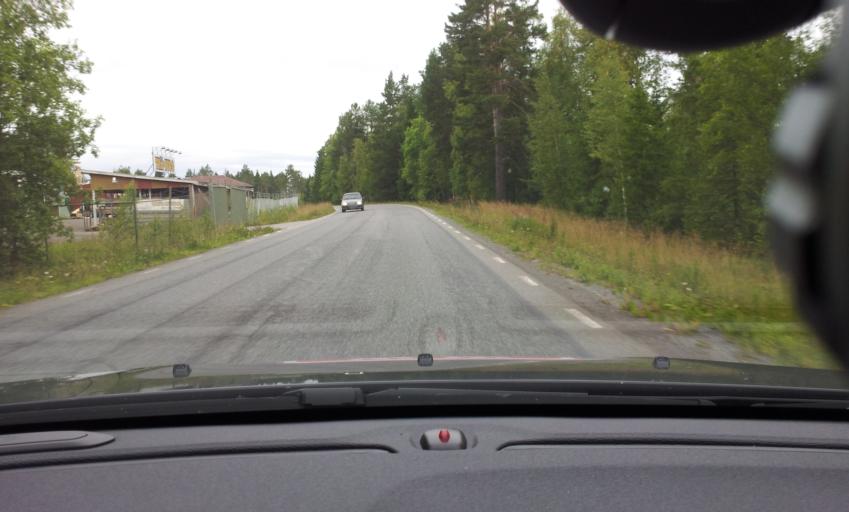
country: SE
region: Jaemtland
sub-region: OEstersunds Kommun
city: Brunflo
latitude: 63.0442
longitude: 14.8679
